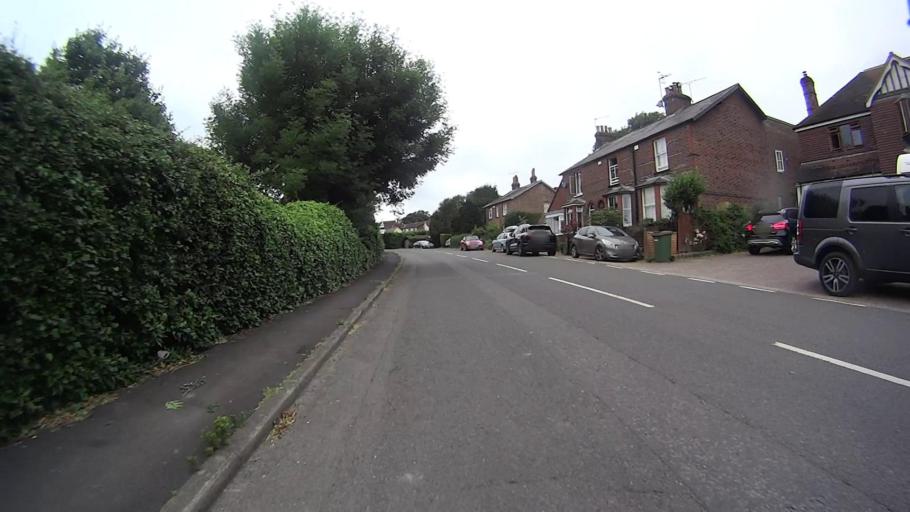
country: GB
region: England
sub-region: Surrey
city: Newdigate
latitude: 51.1575
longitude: -0.3190
